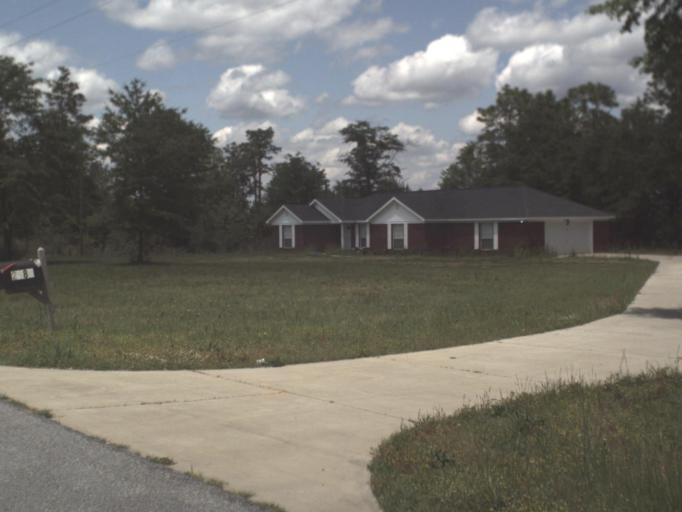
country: US
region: Florida
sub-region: Escambia County
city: Molino
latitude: 30.7720
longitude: -87.3922
